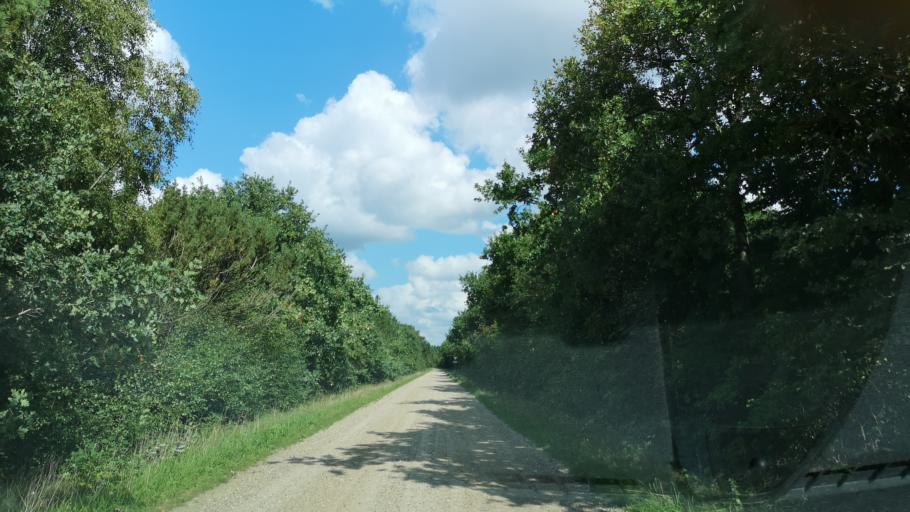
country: DK
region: Central Jutland
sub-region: Ringkobing-Skjern Kommune
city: Skjern
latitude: 55.8641
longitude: 8.3882
